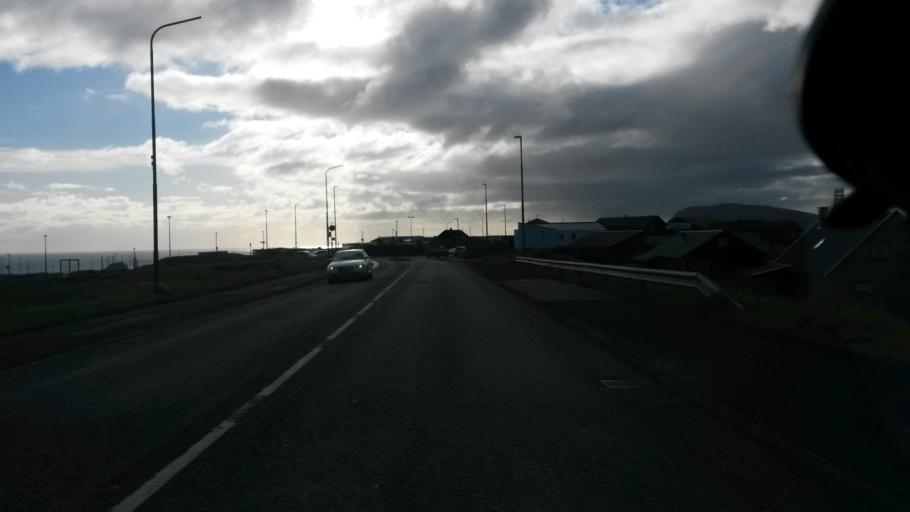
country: FO
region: Streymoy
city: Hoyvik
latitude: 62.0216
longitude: -6.7840
